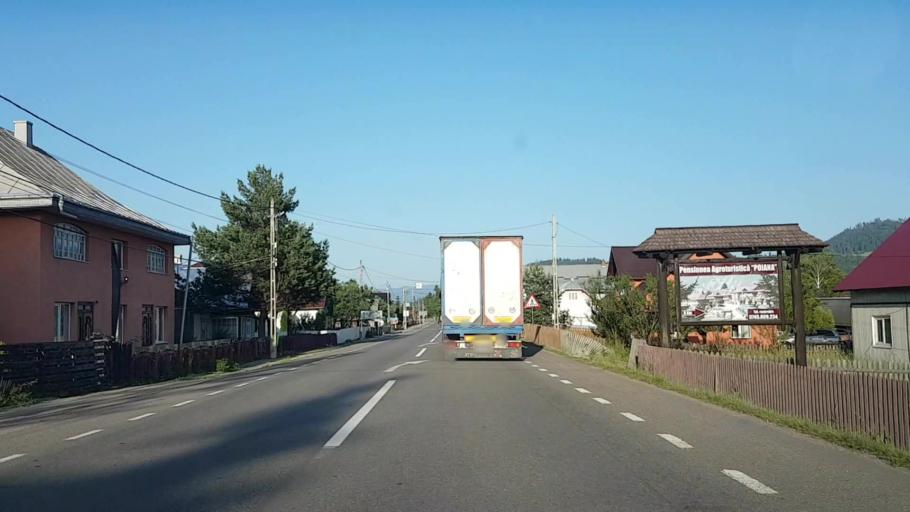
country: RO
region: Suceava
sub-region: Comuna Dorna Candrenilor
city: Dorna Candrenilor
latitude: 47.3563
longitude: 25.2412
